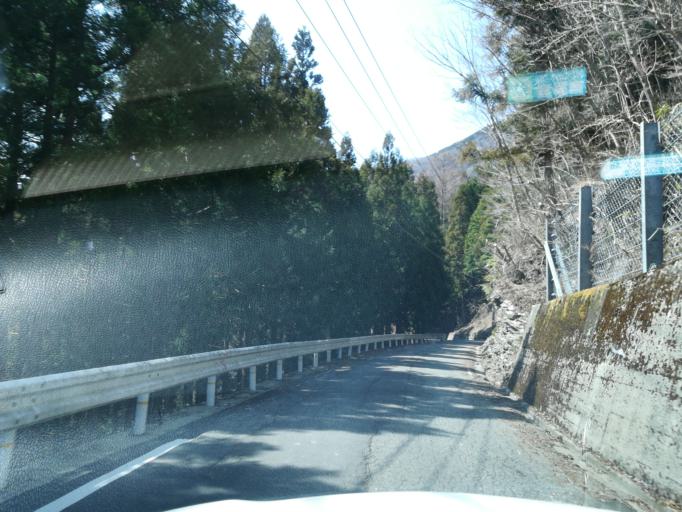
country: JP
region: Tokushima
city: Wakimachi
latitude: 33.8579
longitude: 134.0574
